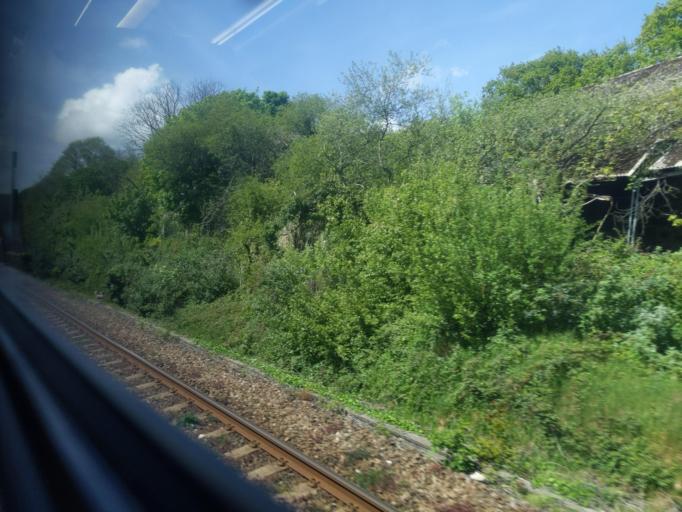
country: GB
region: England
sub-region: Cornwall
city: St Austell
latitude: 50.3432
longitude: -4.8032
